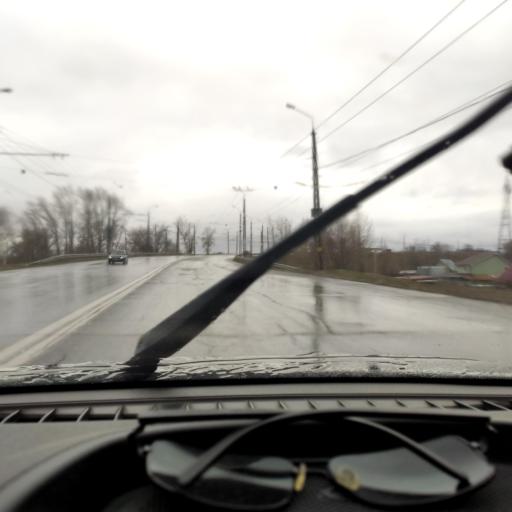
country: RU
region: Samara
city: Zhigulevsk
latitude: 53.4900
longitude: 49.5029
